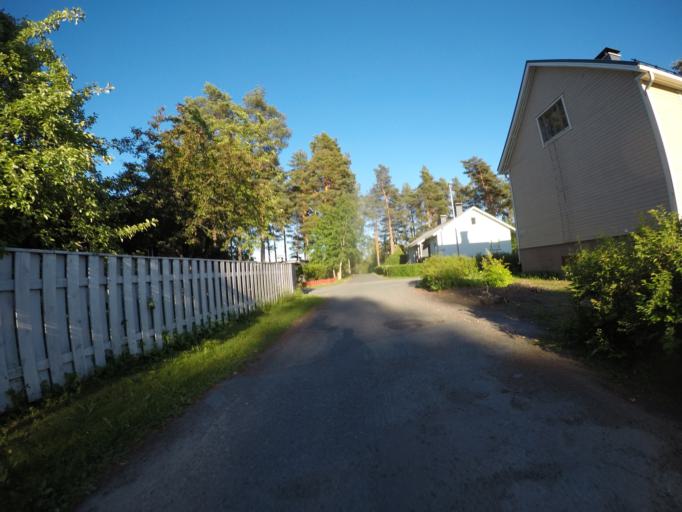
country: FI
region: Haeme
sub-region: Haemeenlinna
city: Haemeenlinna
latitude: 60.9843
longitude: 24.4490
